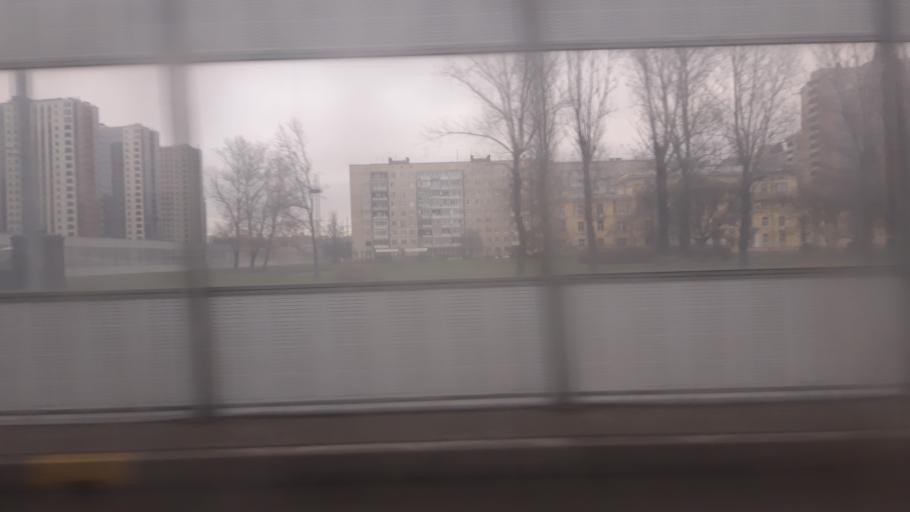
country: RU
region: St.-Petersburg
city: Kupchino
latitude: 59.8294
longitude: 30.3230
